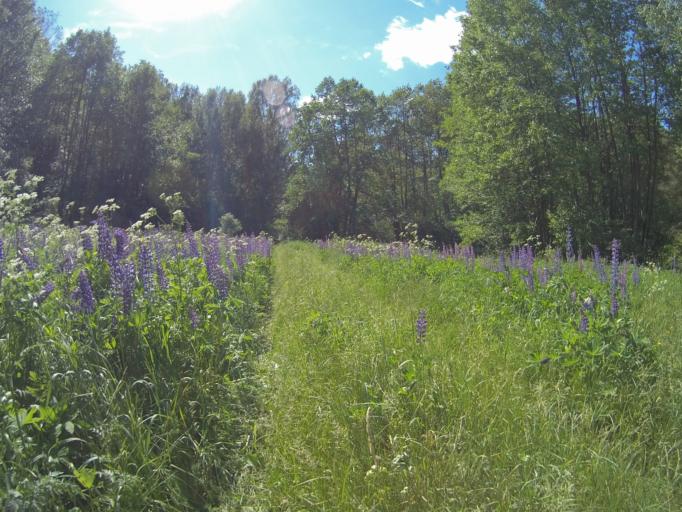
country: RU
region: Vladimir
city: Golovino
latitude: 55.9929
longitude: 40.4124
